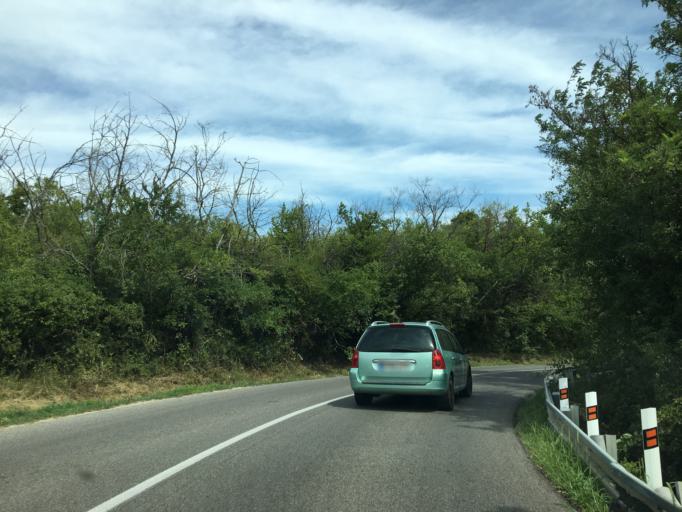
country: HU
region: Komarom-Esztergom
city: Esztergom
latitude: 47.8619
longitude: 18.7421
